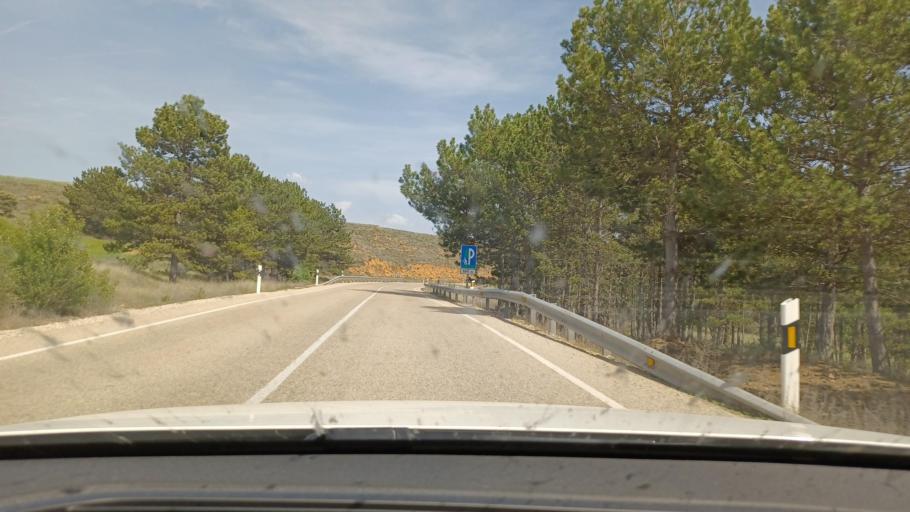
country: ES
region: Castille and Leon
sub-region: Provincia de Soria
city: Monteagudo de las Vicarias
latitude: 41.3968
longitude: -2.2017
